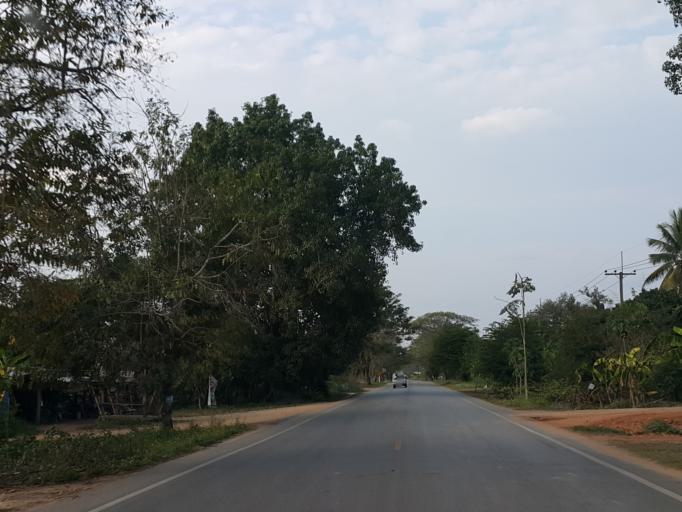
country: TH
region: Lampang
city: Lampang
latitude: 18.4929
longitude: 99.4719
